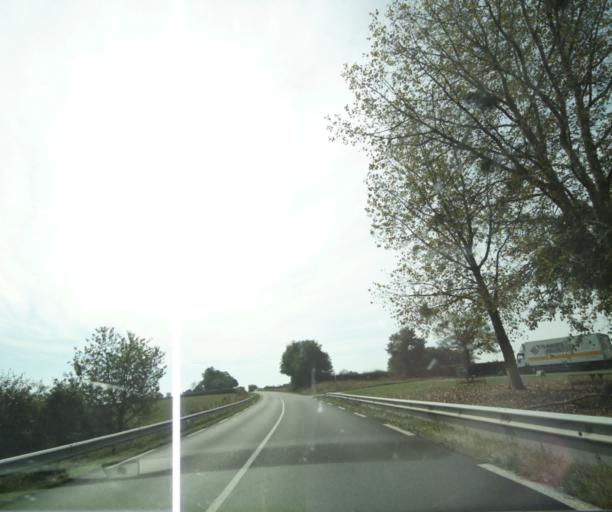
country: FR
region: Auvergne
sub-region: Departement de l'Allier
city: Saint-Francois
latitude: 46.4340
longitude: 3.9074
